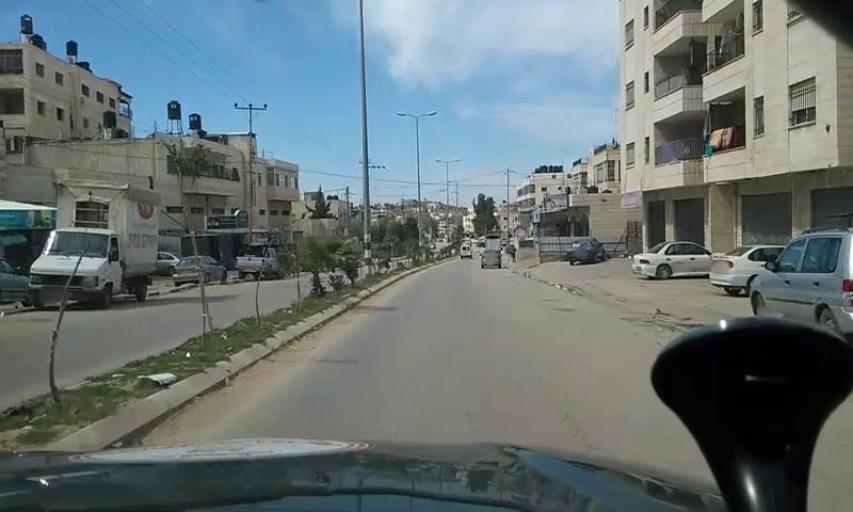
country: PS
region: West Bank
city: Bir Nabala
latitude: 31.8519
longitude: 35.1995
